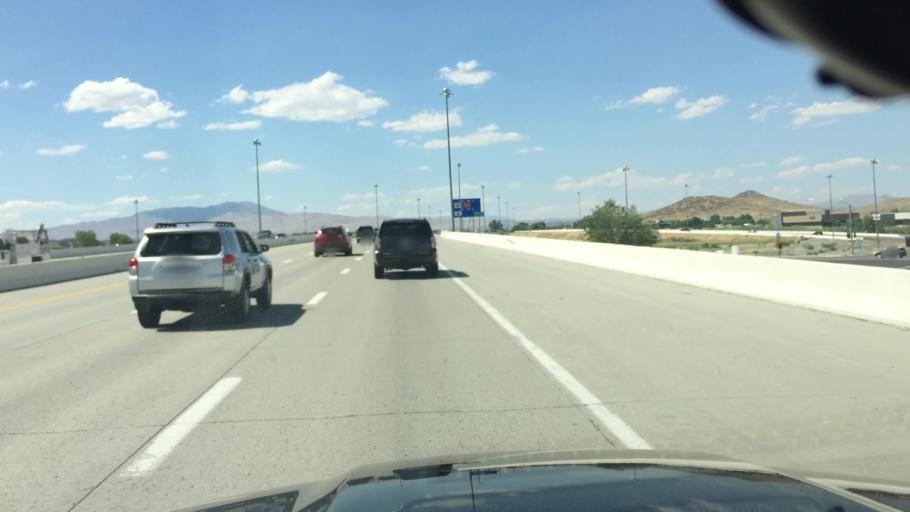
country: US
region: Nevada
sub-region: Washoe County
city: Sparks
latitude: 39.4373
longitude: -119.7639
